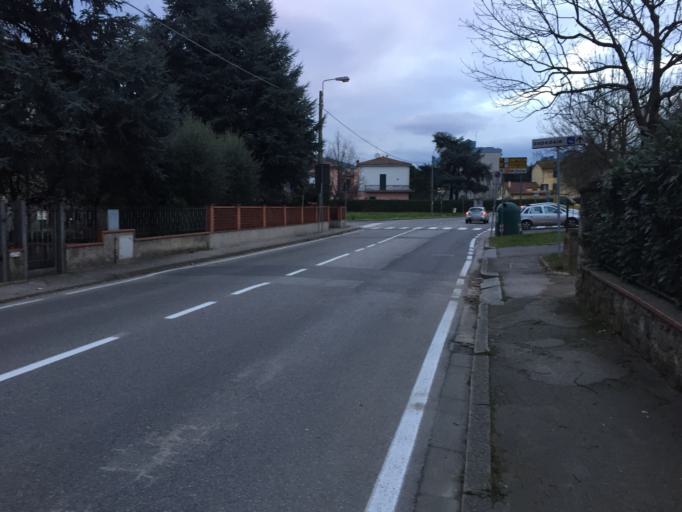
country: IT
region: Tuscany
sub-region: Provincia di Prato
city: Fornacelle
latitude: 43.8863
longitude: 11.0466
